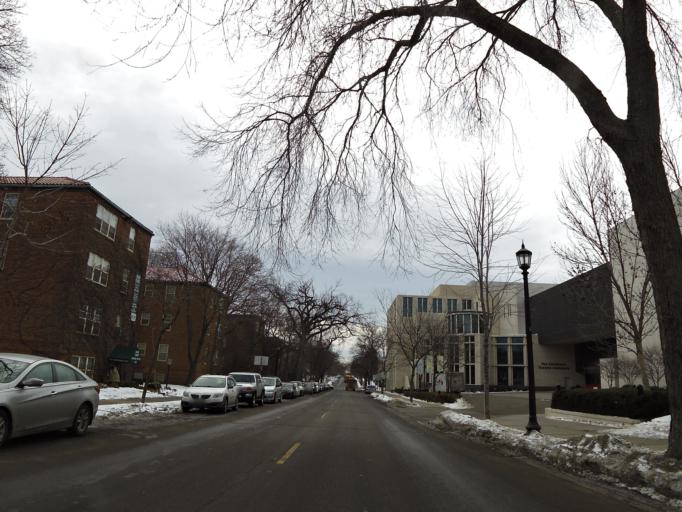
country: US
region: Minnesota
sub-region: Hennepin County
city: Minneapolis
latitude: 44.9590
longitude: -93.2727
